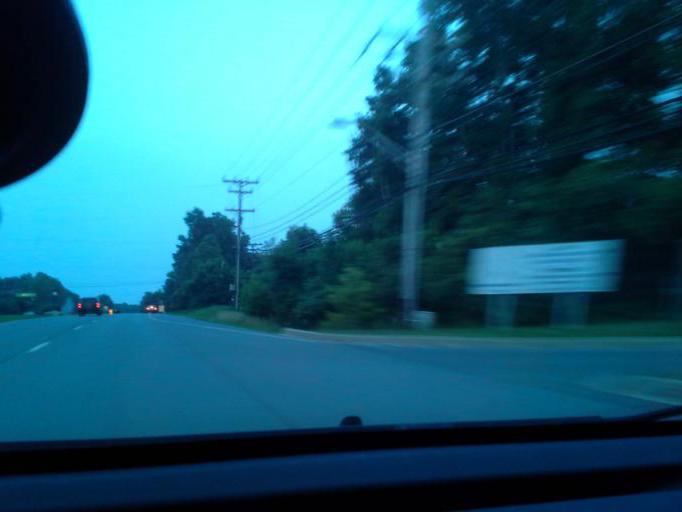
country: US
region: Maryland
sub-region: Calvert County
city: Chesapeake Beach
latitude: 38.6990
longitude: -76.5518
